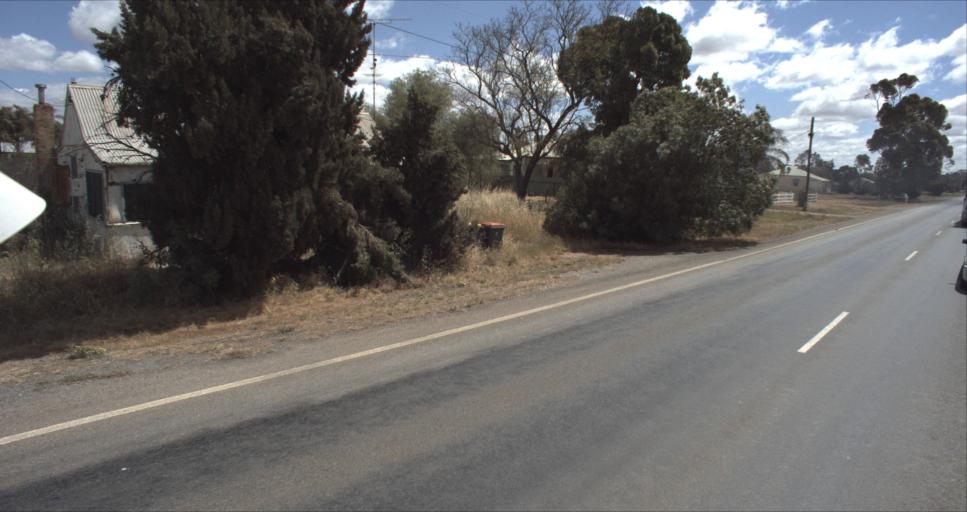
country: AU
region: New South Wales
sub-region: Murrumbidgee Shire
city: Darlington Point
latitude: -34.5152
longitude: 146.1855
